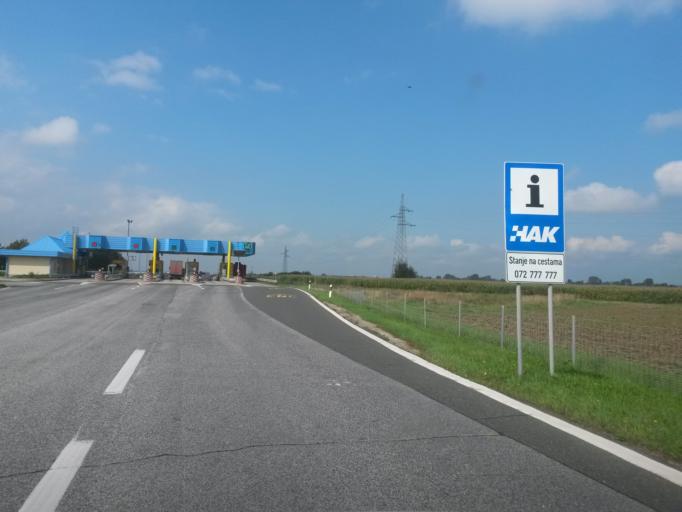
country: HR
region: Medimurska
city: Kursanec
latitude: 46.2622
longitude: 16.3970
